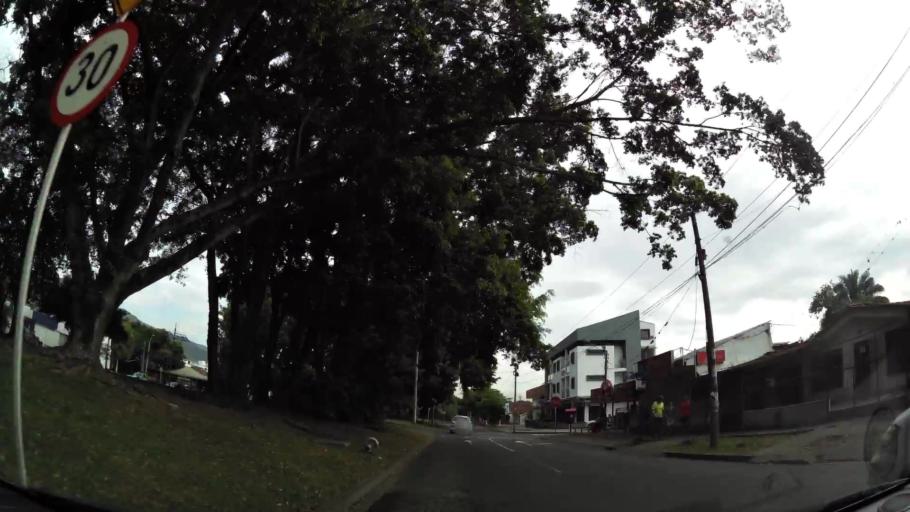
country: CO
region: Valle del Cauca
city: Cali
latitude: 3.4826
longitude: -76.5211
